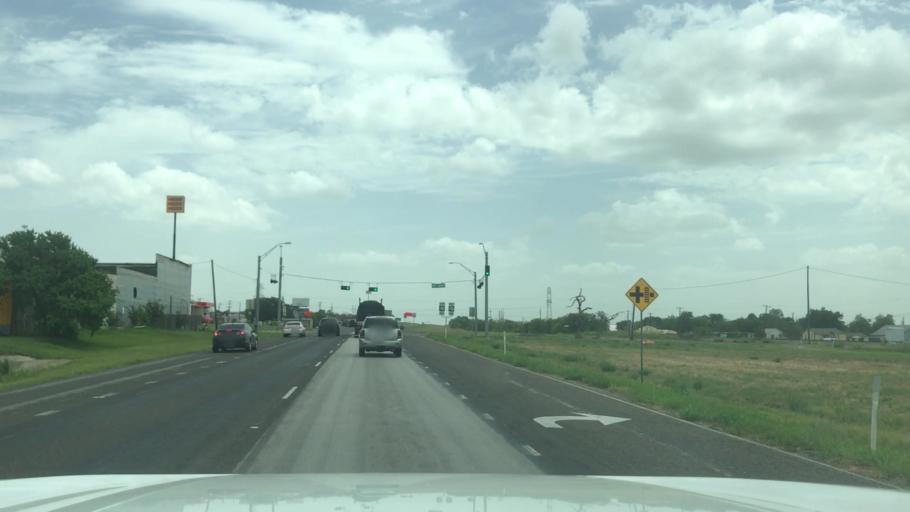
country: US
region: Texas
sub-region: McLennan County
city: Riesel
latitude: 31.4757
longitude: -96.9260
